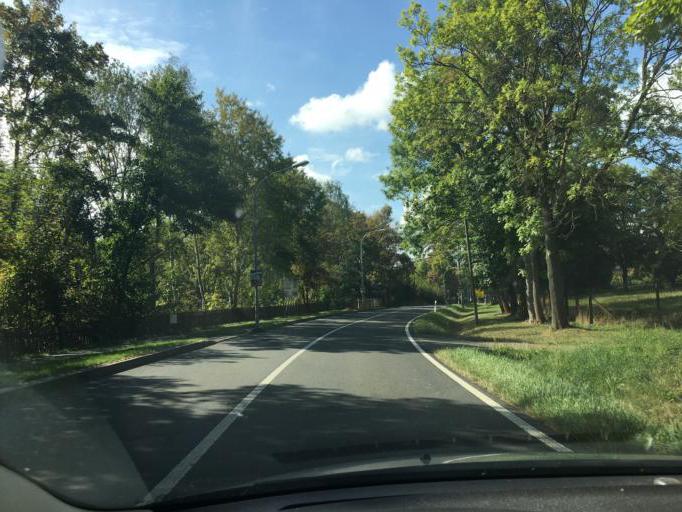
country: DE
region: Thuringia
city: Auma
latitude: 50.7064
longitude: 11.8973
